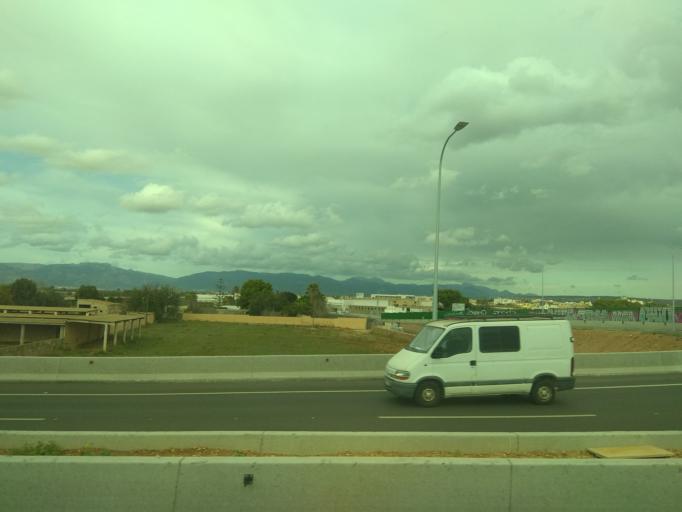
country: ES
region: Balearic Islands
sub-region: Illes Balears
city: Palma
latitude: 39.5684
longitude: 2.7095
